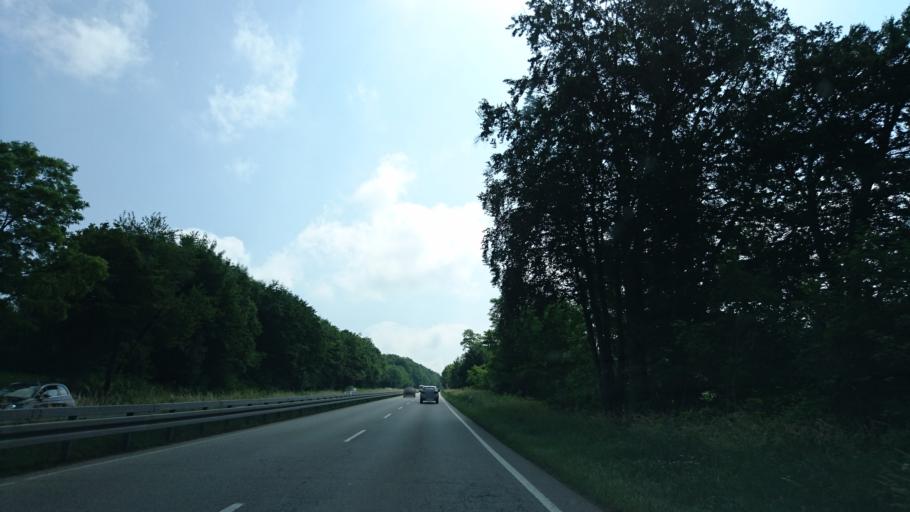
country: DE
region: Bavaria
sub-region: Swabia
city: Diedorf
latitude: 48.3705
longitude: 10.8057
